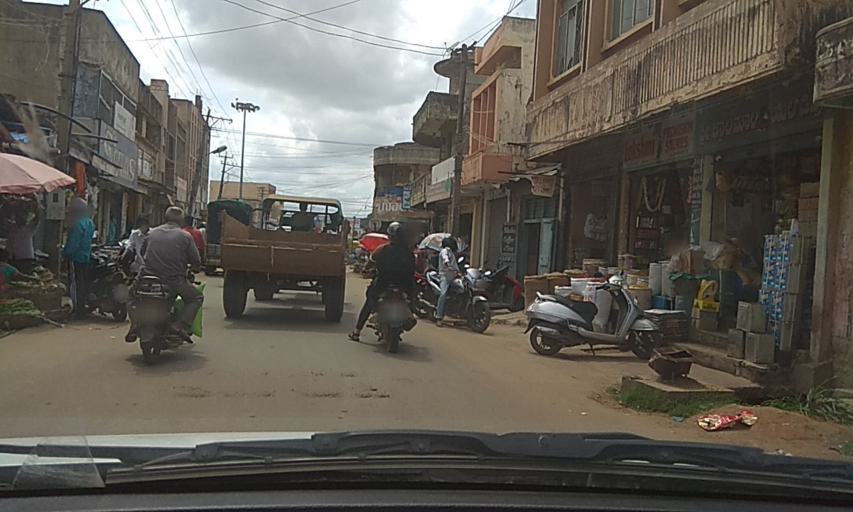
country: IN
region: Karnataka
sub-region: Tumkur
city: Tumkur
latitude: 13.3450
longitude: 77.1001
